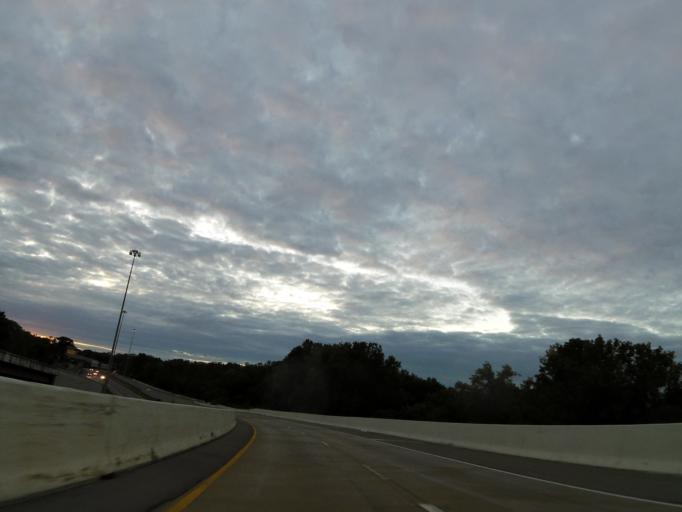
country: US
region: Tennessee
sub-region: Davidson County
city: Belle Meade
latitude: 36.1562
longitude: -86.8582
